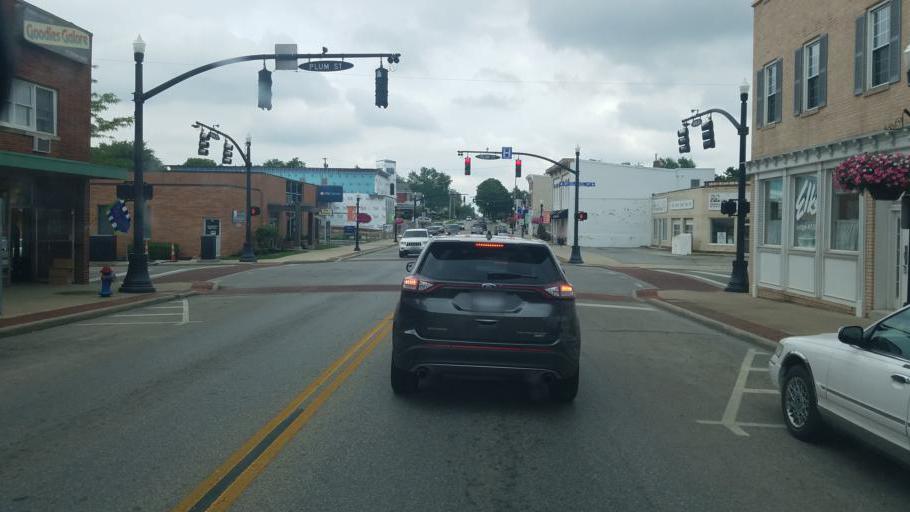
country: US
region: Ohio
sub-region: Union County
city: Marysville
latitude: 40.2364
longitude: -83.3661
